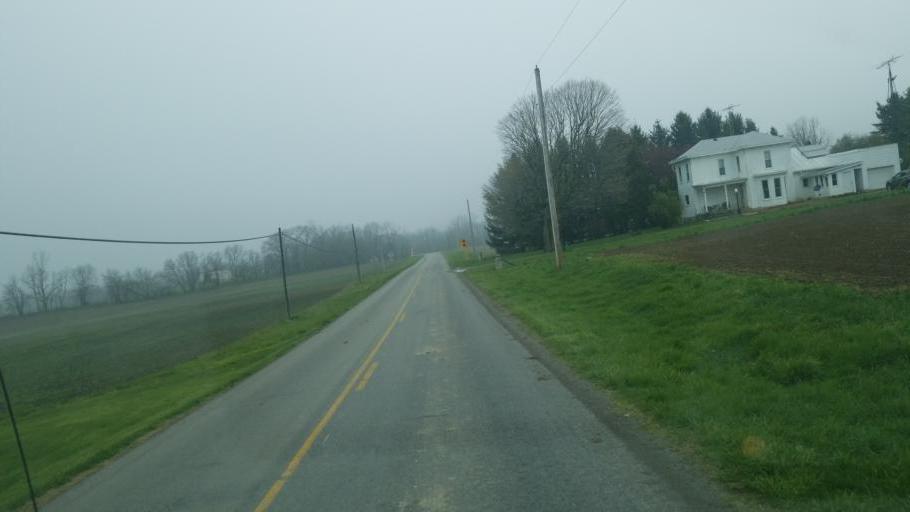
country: US
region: Ohio
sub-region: Logan County
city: De Graff
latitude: 40.3482
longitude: -83.9312
